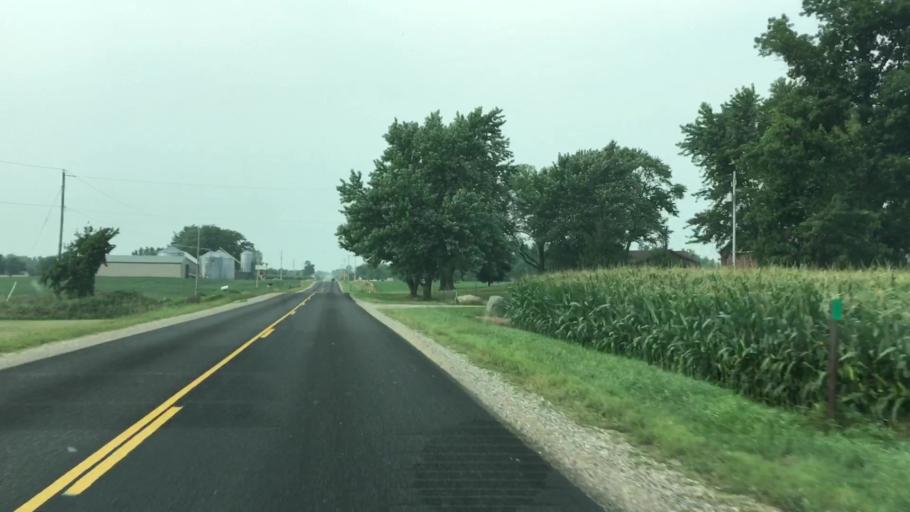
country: US
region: Michigan
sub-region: Ottawa County
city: Hudsonville
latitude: 42.8072
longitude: -85.9007
